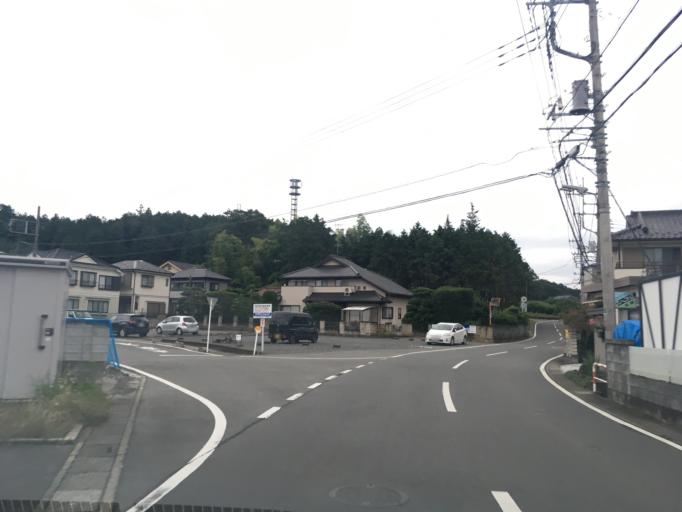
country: JP
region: Saitama
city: Sayama
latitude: 35.8298
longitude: 139.3705
